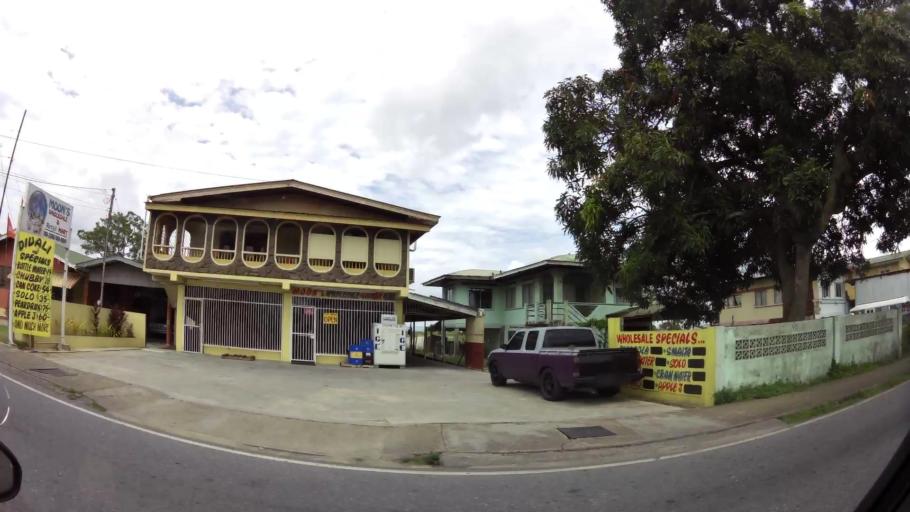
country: TT
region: Couva-Tabaquite-Talparo
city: Couva
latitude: 10.4396
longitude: -61.4521
